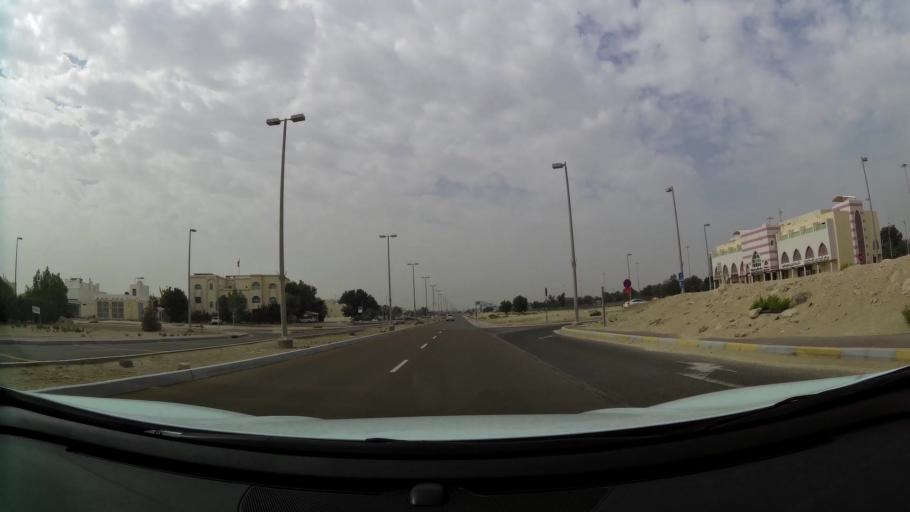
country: AE
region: Abu Dhabi
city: Abu Dhabi
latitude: 24.3234
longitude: 54.6196
